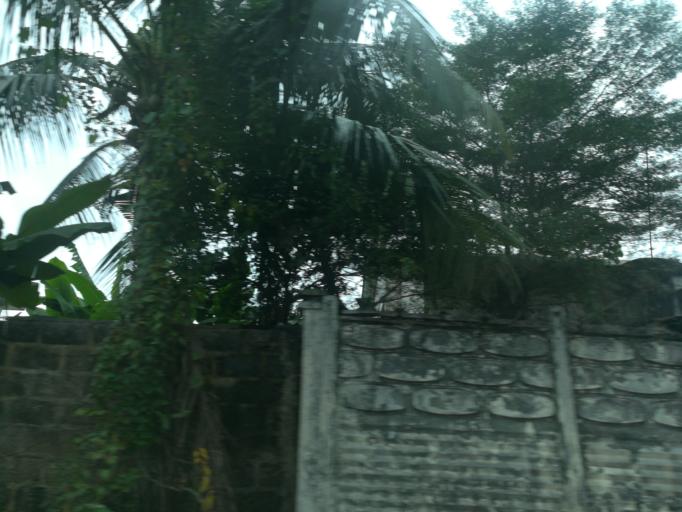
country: NG
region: Rivers
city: Port Harcourt
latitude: 4.8413
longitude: 7.0357
